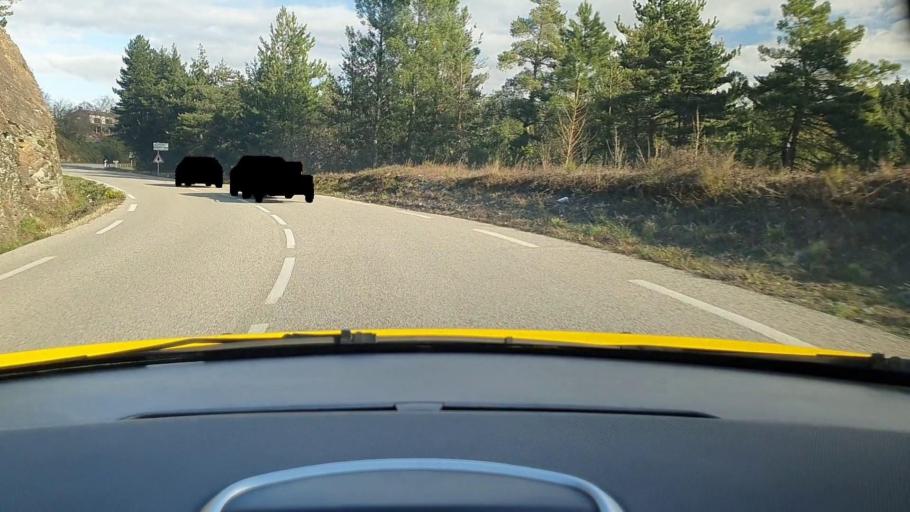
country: FR
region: Languedoc-Roussillon
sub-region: Departement du Gard
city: Branoux-les-Taillades
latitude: 44.3648
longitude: 3.9482
